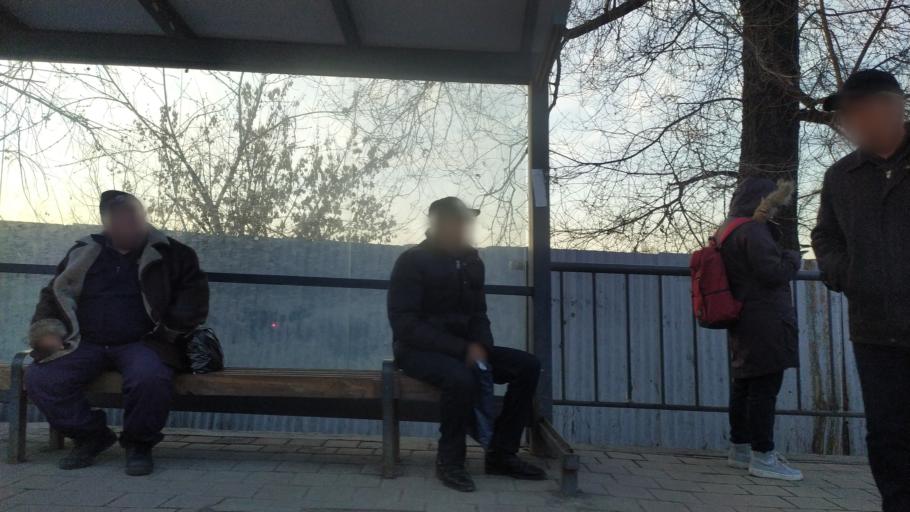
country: KZ
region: Almaty Qalasy
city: Almaty
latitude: 43.2235
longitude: 76.8859
